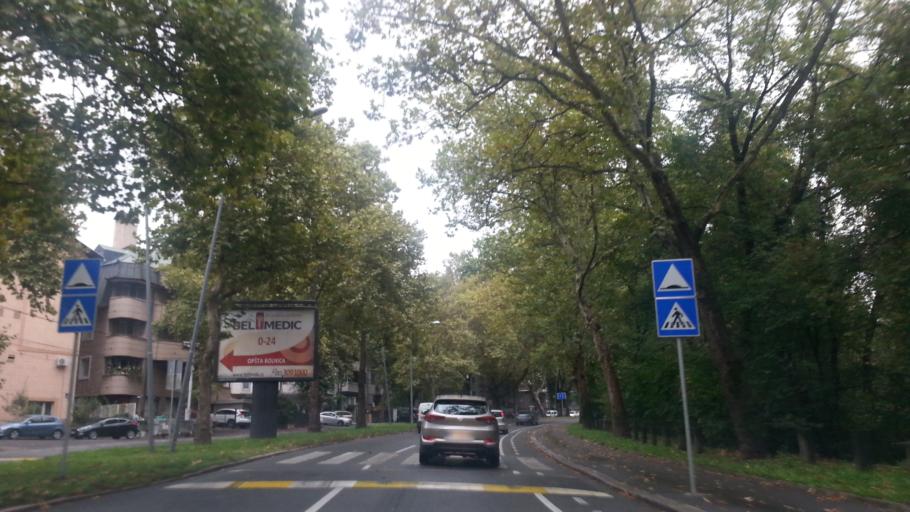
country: RS
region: Central Serbia
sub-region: Belgrade
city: Vozdovac
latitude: 44.7774
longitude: 20.4715
